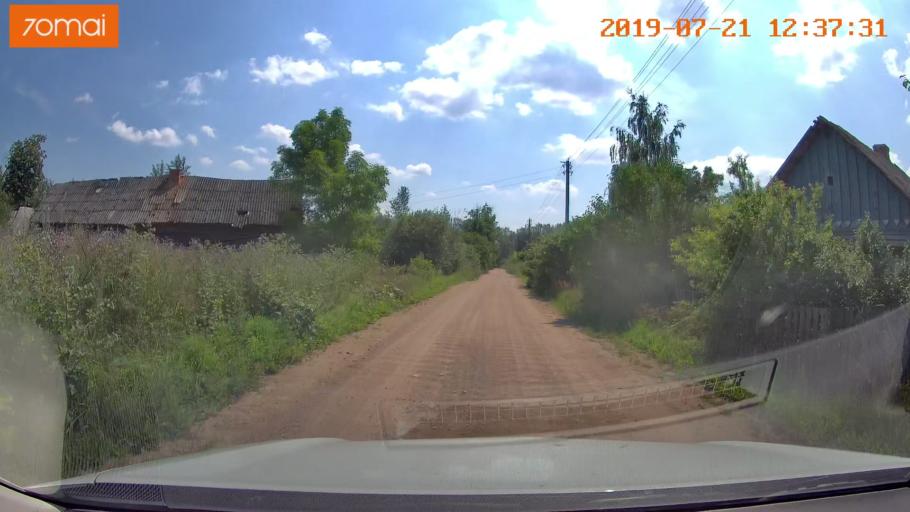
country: BY
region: Grodnenskaya
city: Lyubcha
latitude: 53.8636
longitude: 26.0066
